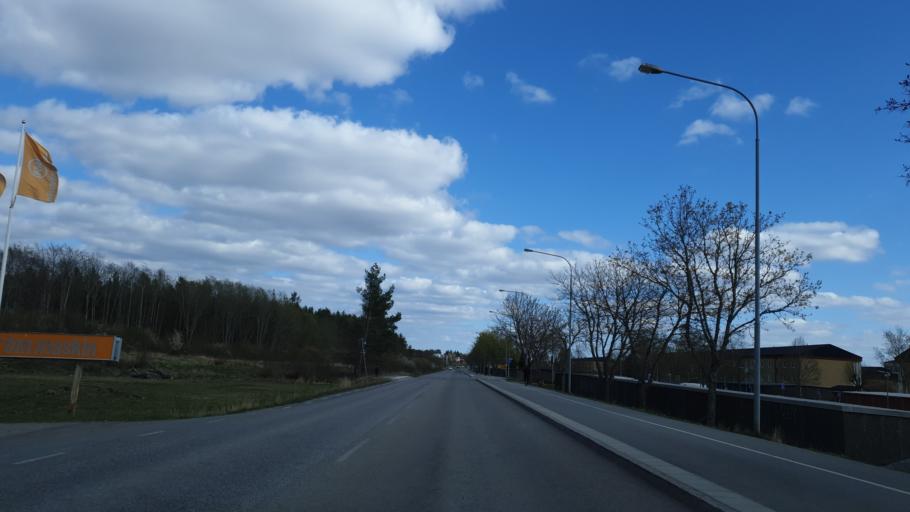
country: SE
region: Uppsala
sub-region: Uppsala Kommun
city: Gamla Uppsala
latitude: 59.8906
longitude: 17.6530
